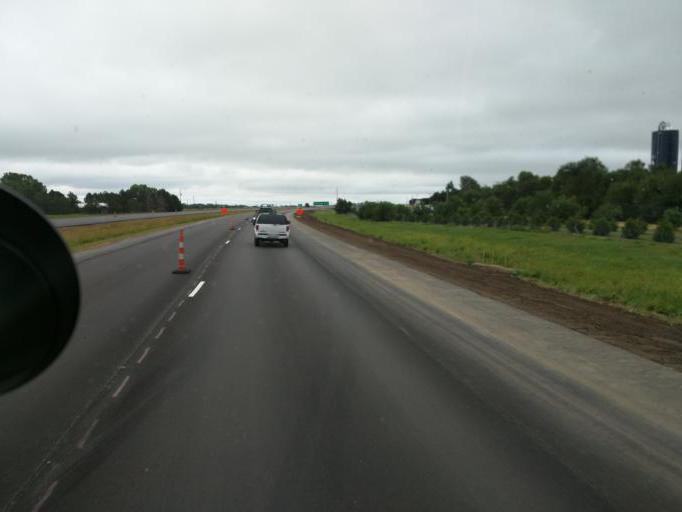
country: US
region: Kansas
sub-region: Reno County
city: South Hutchinson
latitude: 38.0139
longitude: -97.9988
